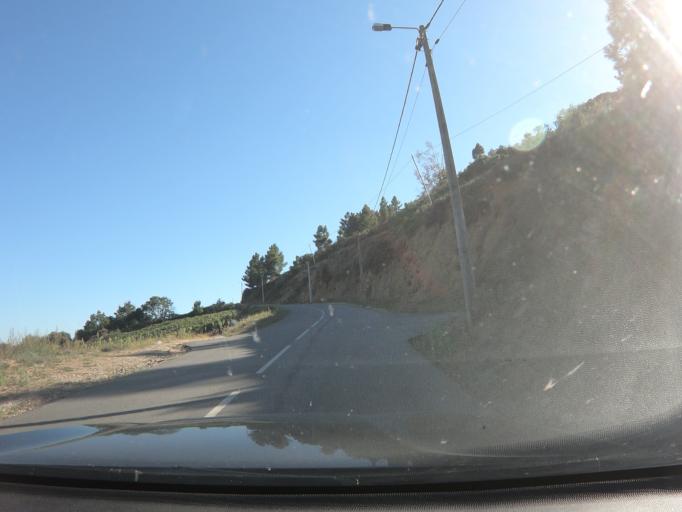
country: PT
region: Vila Real
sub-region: Sabrosa
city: Vilela
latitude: 41.2245
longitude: -7.5630
